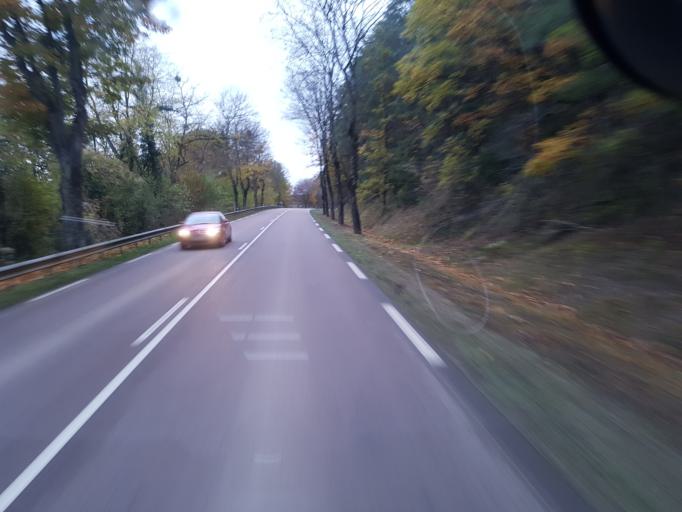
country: FR
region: Champagne-Ardenne
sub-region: Departement de l'Aube
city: Mussy-sur-Seine
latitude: 47.9996
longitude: 4.4771
